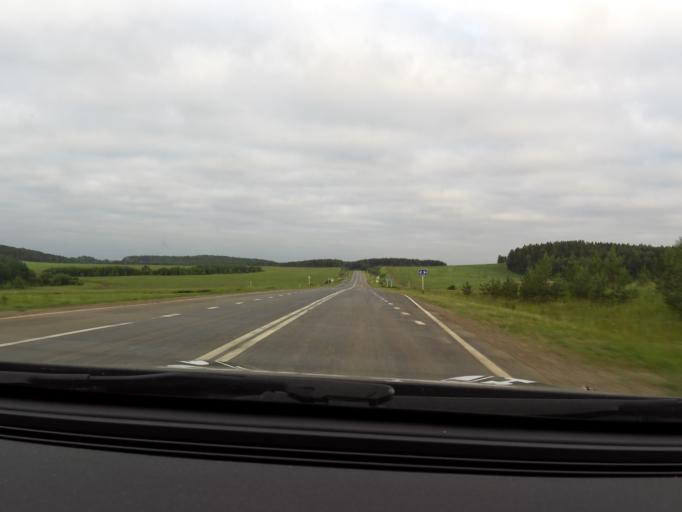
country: RU
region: Perm
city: Siva
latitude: 58.4159
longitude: 54.4643
